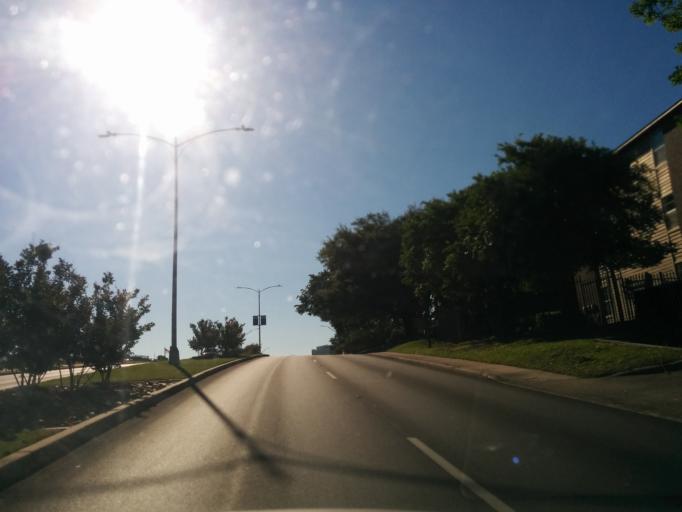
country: US
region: Texas
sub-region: Bexar County
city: Leon Valley
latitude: 29.5110
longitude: -98.5834
